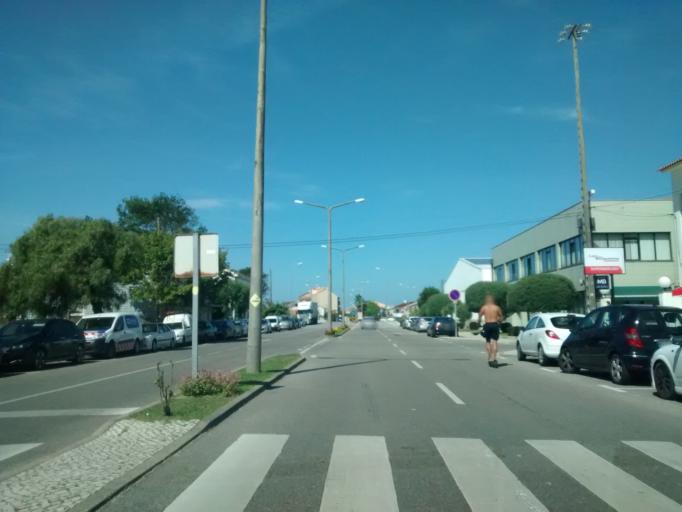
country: PT
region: Coimbra
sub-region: Mira
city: Mira
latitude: 40.4554
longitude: -8.7880
